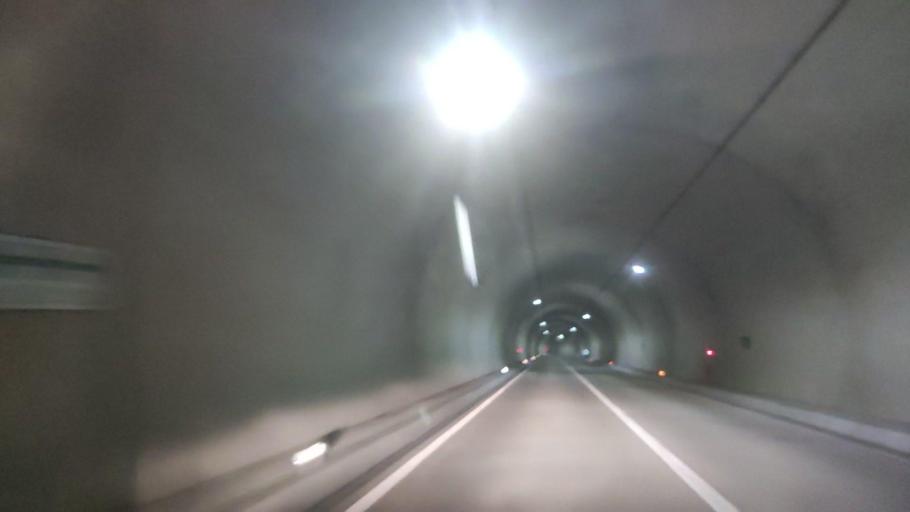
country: JP
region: Tottori
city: Tottori
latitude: 35.3527
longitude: 134.4732
